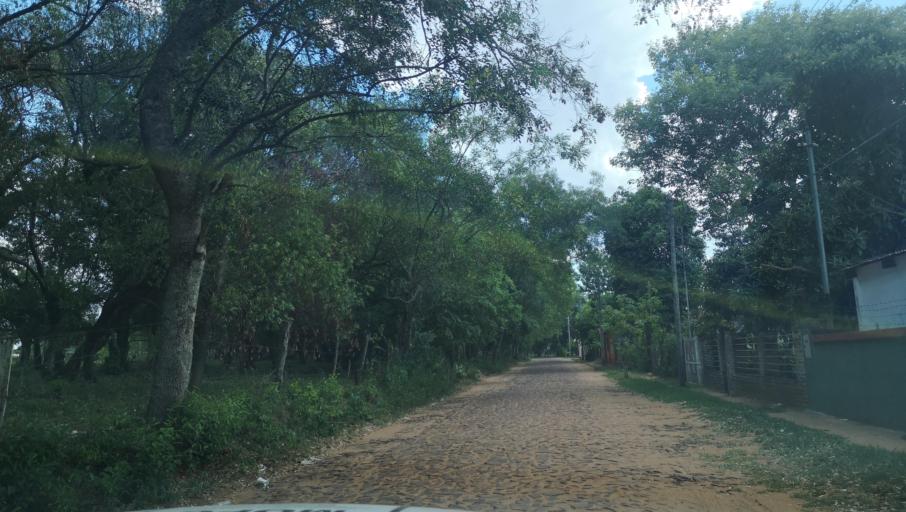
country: PY
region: Misiones
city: Santa Maria
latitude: -26.8891
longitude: -57.0108
